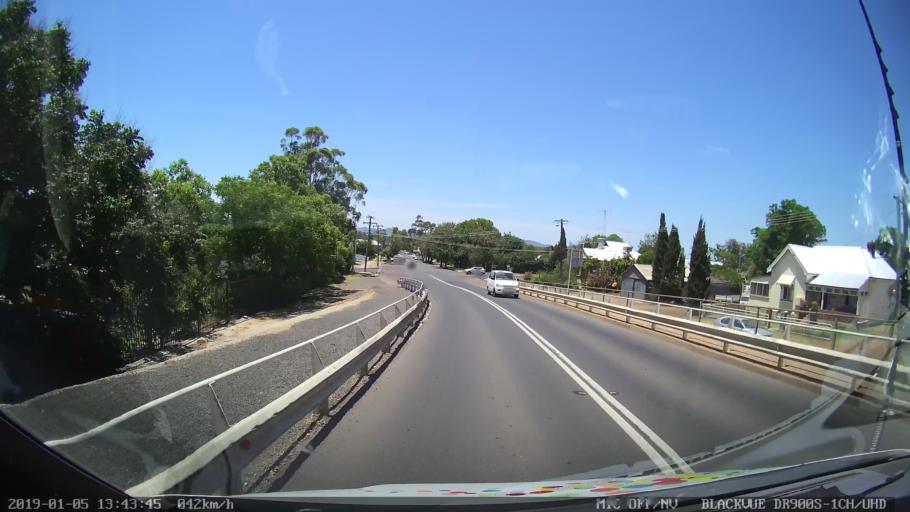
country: AU
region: New South Wales
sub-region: Gunnedah
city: Gunnedah
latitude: -30.9816
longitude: 150.2542
